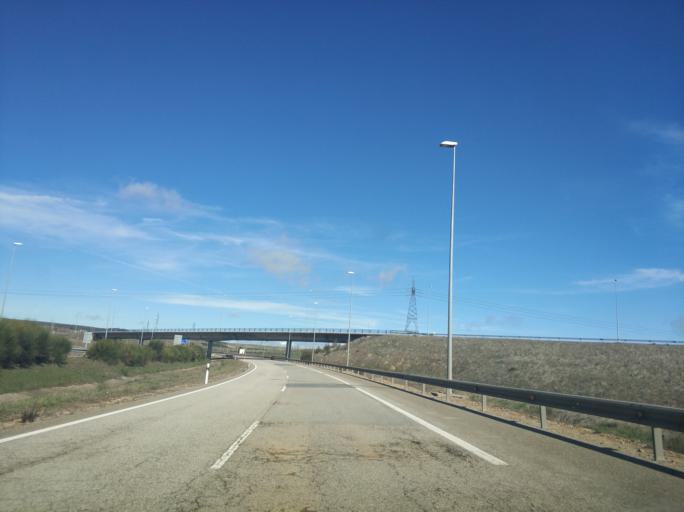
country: ES
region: Castille and Leon
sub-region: Provincia de Burgos
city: Burgos
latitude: 42.3696
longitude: -3.6402
